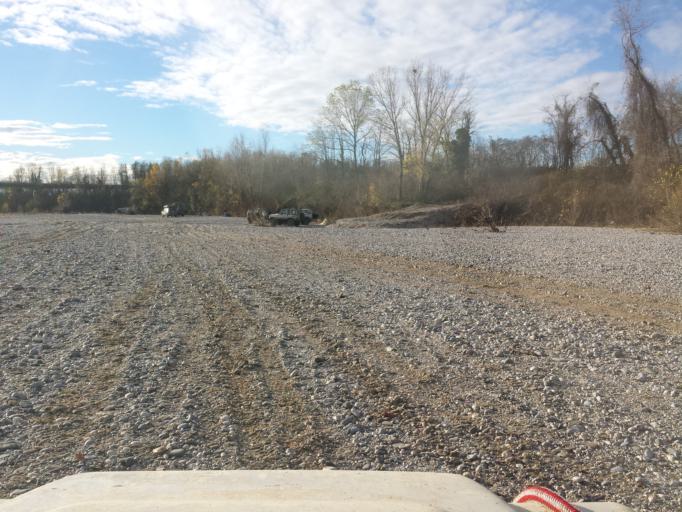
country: IT
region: Friuli Venezia Giulia
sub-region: Provincia di Udine
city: San Vito al Torre
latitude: 45.8958
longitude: 13.4028
